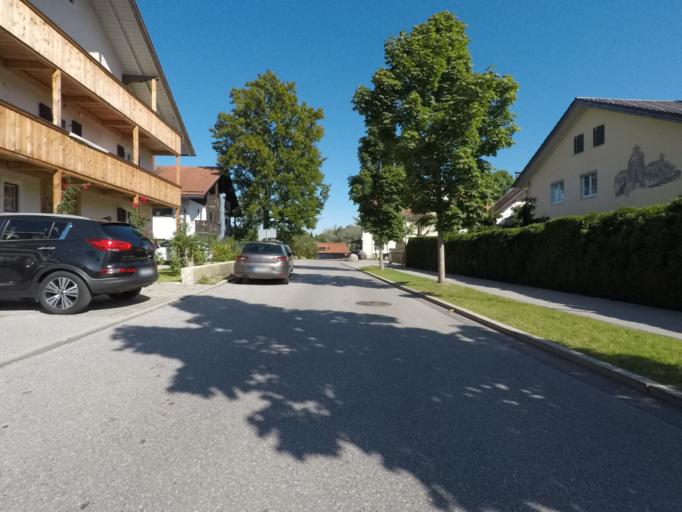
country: DE
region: Bavaria
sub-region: Upper Bavaria
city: Bad Toelz
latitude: 47.7623
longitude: 11.5481
